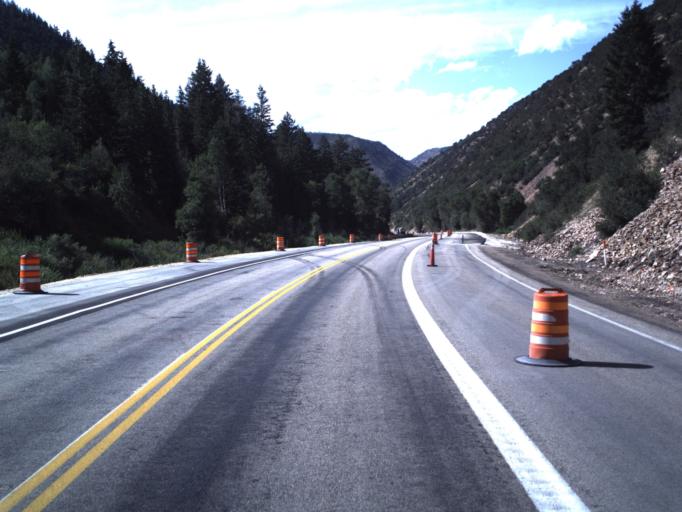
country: US
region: Utah
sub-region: Wasatch County
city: Heber
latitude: 40.3580
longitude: -111.2834
